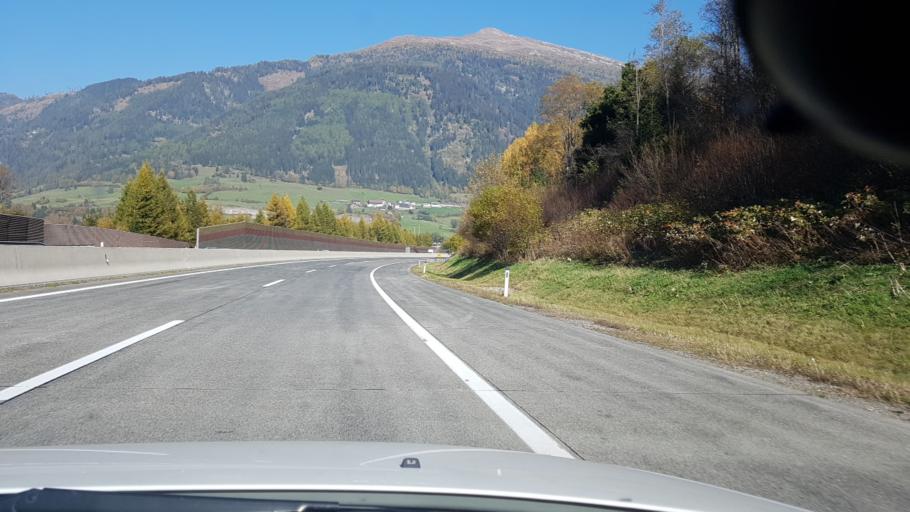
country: AT
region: Salzburg
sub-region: Politischer Bezirk Tamsweg
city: Sankt Michael im Lungau
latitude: 47.0872
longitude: 13.6070
